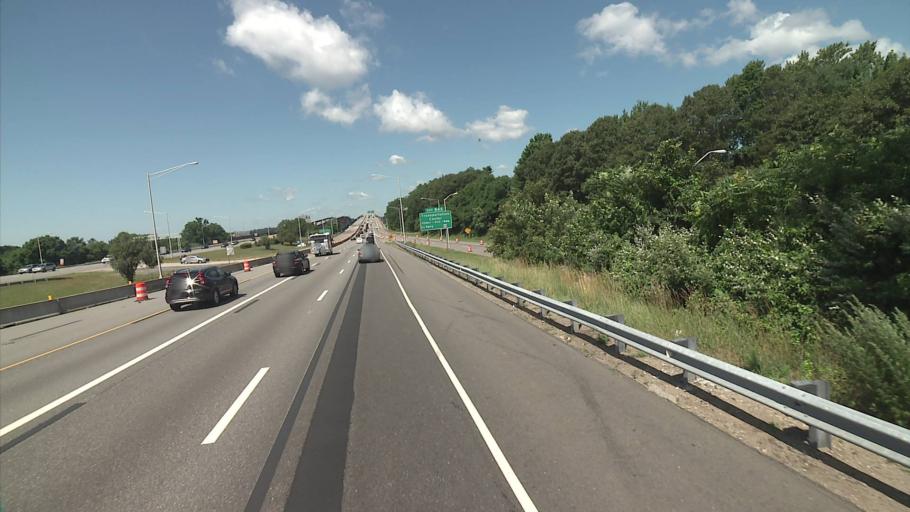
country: US
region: Connecticut
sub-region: New London County
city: Groton
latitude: 41.3649
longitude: -72.0758
